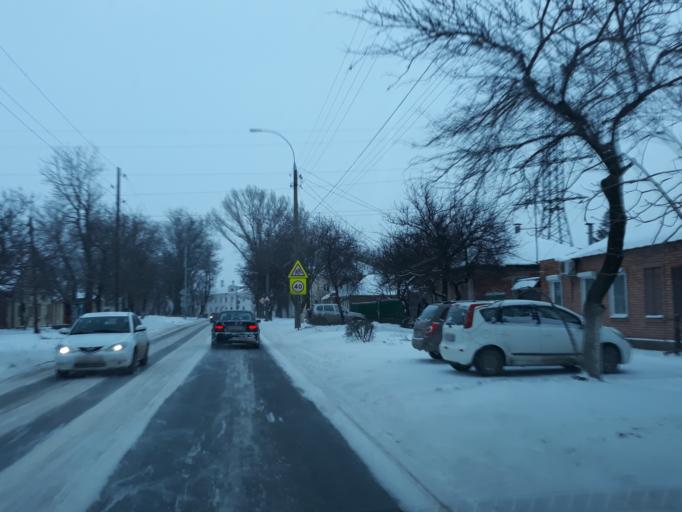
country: RU
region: Rostov
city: Taganrog
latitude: 47.2590
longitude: 38.9390
